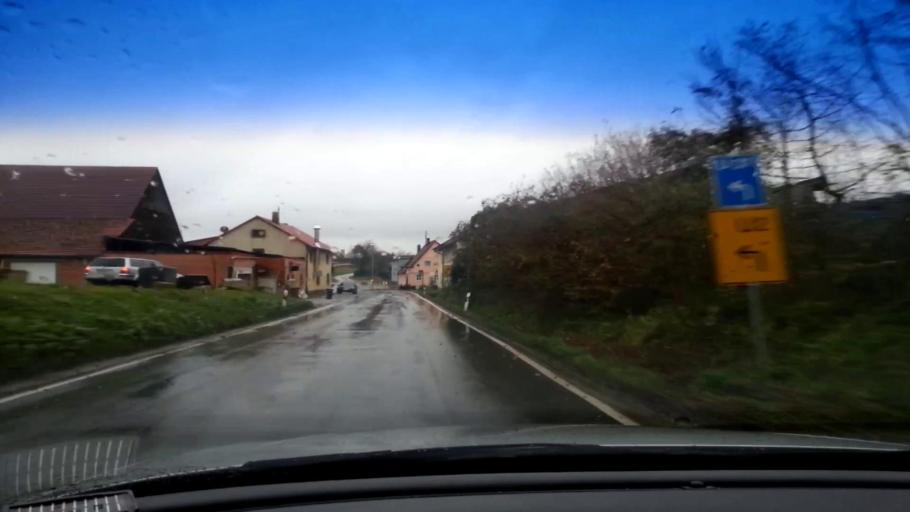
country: DE
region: Bavaria
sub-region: Upper Franconia
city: Schesslitz
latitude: 49.9545
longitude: 11.0202
